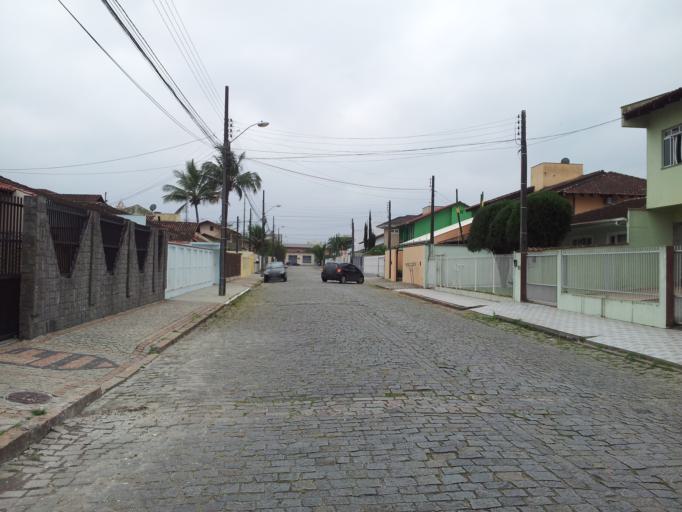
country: BR
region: Santa Catarina
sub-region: Joinville
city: Joinville
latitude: -26.3205
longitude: -48.8411
